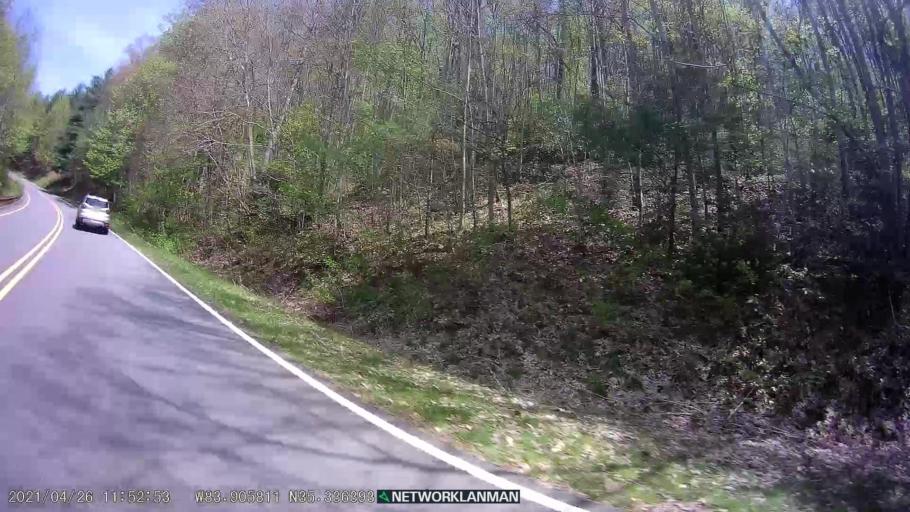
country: US
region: North Carolina
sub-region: Graham County
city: Robbinsville
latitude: 35.3364
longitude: -83.9056
